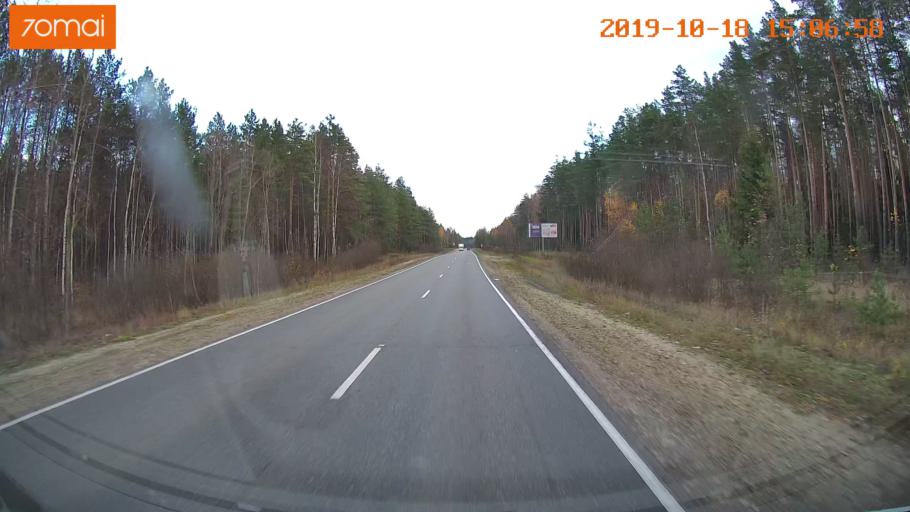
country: RU
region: Vladimir
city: Gus'-Khrustal'nyy
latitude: 55.5357
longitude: 40.5873
